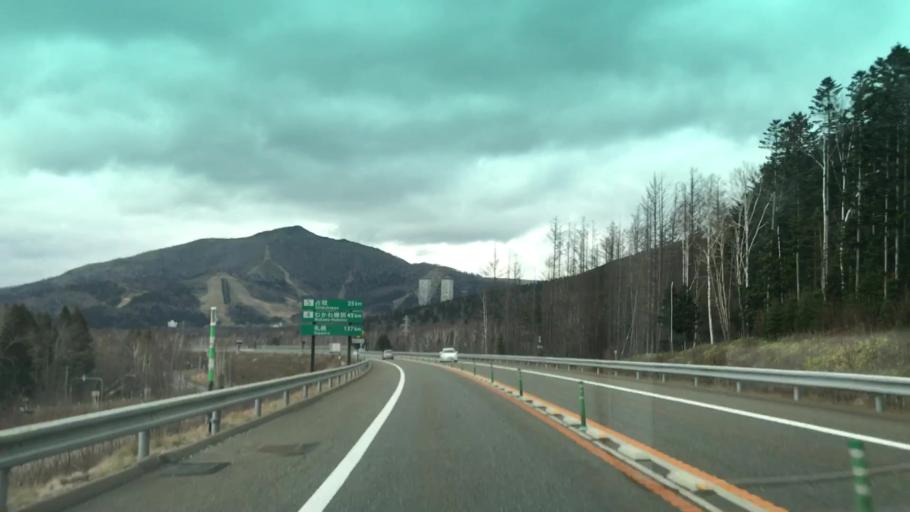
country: JP
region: Hokkaido
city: Shimo-furano
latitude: 43.0504
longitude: 142.6490
